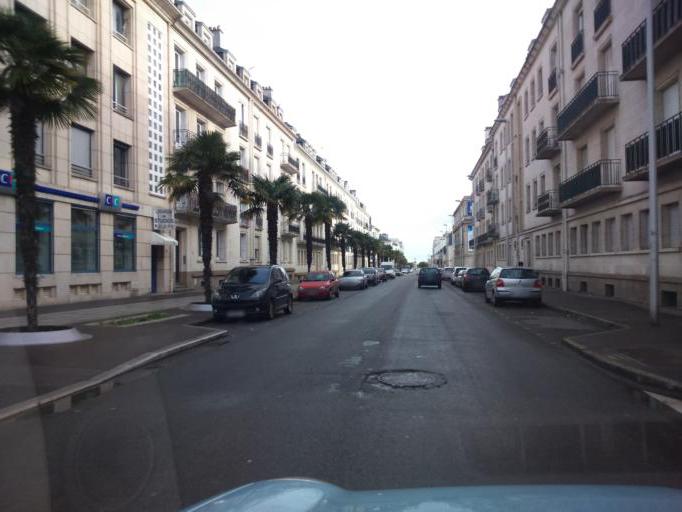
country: FR
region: Pays de la Loire
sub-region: Departement de la Loire-Atlantique
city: Saint-Nazaire
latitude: 47.2738
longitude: -2.2099
